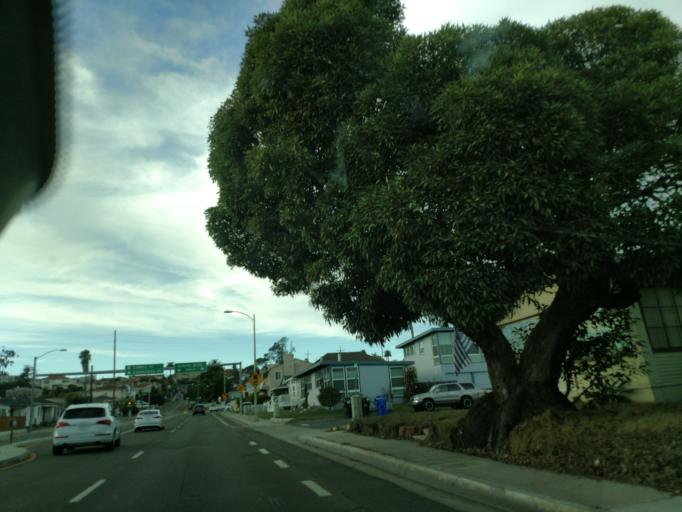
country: US
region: California
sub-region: San Diego County
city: Coronado
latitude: 32.7291
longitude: -117.2266
